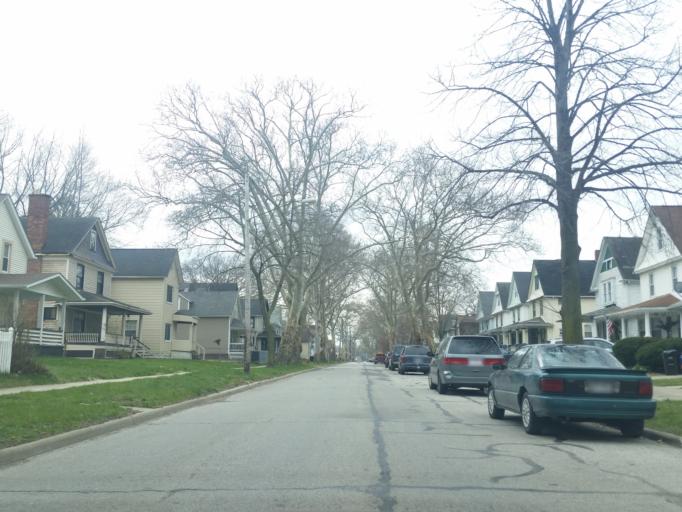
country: US
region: Ohio
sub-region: Cuyahoga County
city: Brooklyn
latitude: 41.4762
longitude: -81.7432
